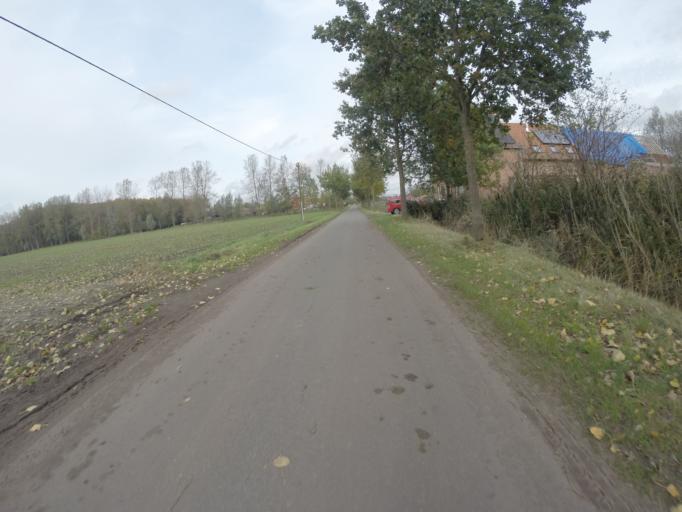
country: BE
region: Flanders
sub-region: Provincie Oost-Vlaanderen
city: Maldegem
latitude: 51.1769
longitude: 3.4273
